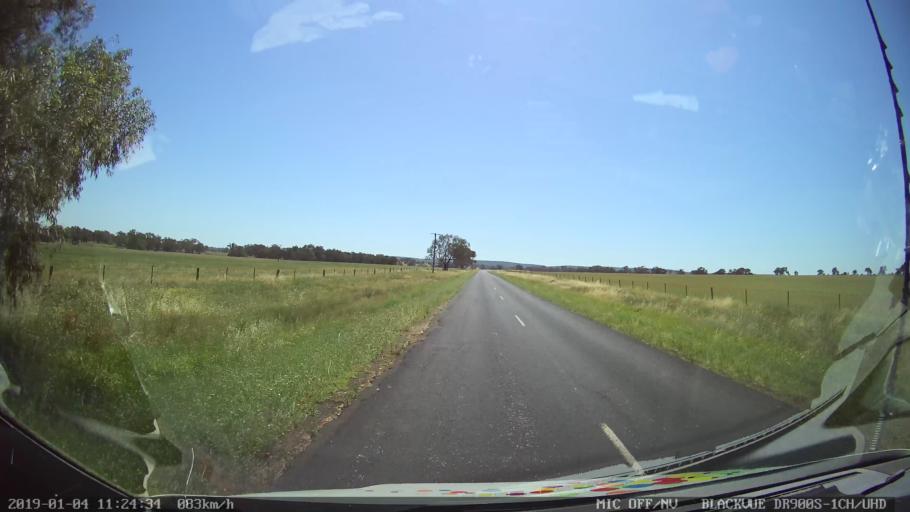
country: AU
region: New South Wales
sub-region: Cabonne
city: Molong
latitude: -33.1318
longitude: 148.7484
